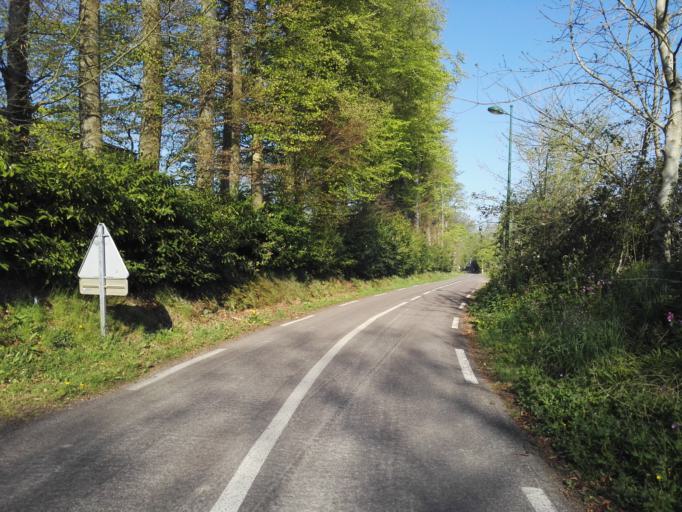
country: FR
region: Haute-Normandie
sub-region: Departement de la Seine-Maritime
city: Doudeville
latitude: 49.7368
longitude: 0.7159
